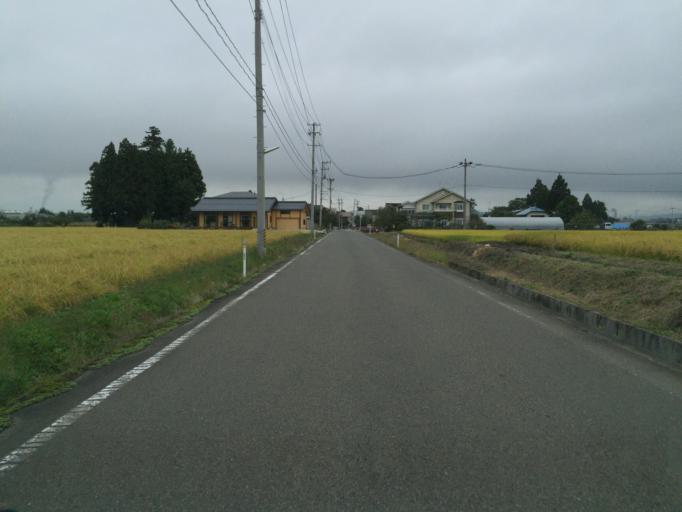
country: JP
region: Fukushima
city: Kitakata
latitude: 37.4663
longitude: 139.9147
